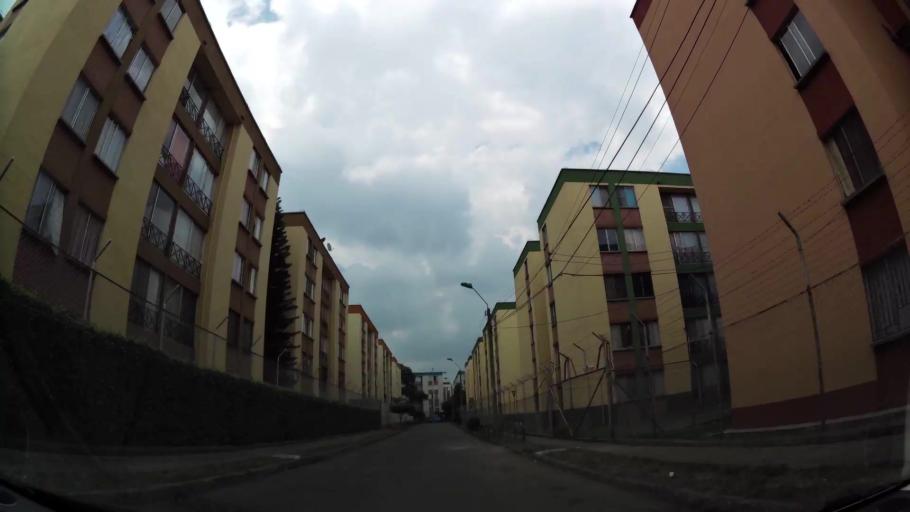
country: CO
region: Valle del Cauca
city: Cali
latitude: 3.4752
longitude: -76.4993
